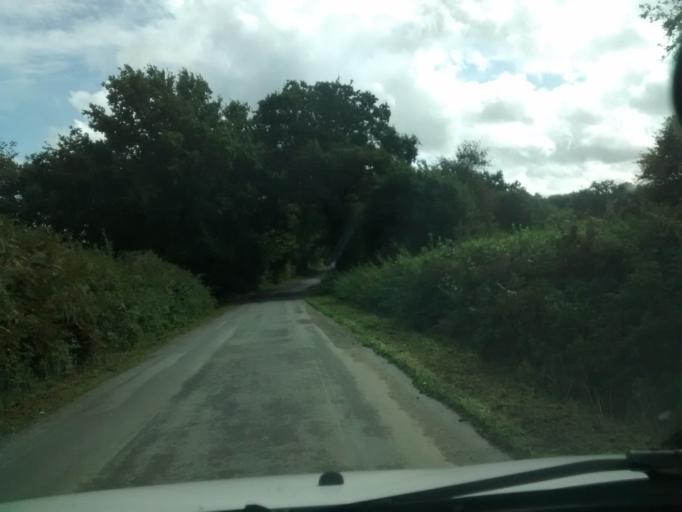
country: FR
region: Brittany
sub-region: Departement d'Ille-et-Vilaine
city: Chateaubourg
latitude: 48.1239
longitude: -1.3927
